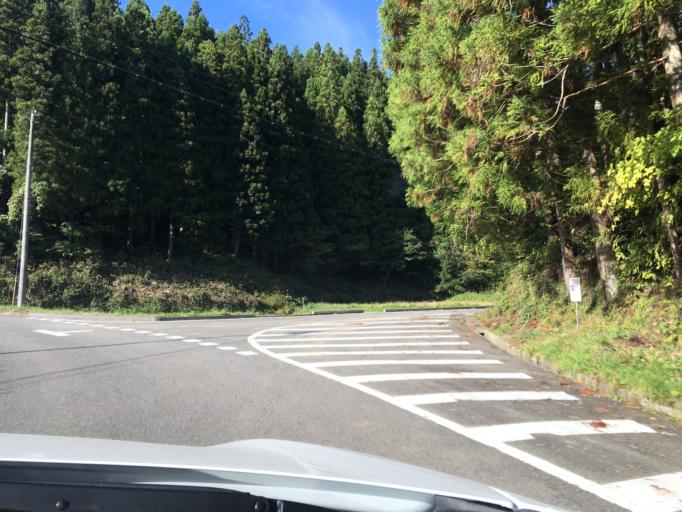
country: JP
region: Fukushima
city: Ishikawa
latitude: 37.1312
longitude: 140.5519
